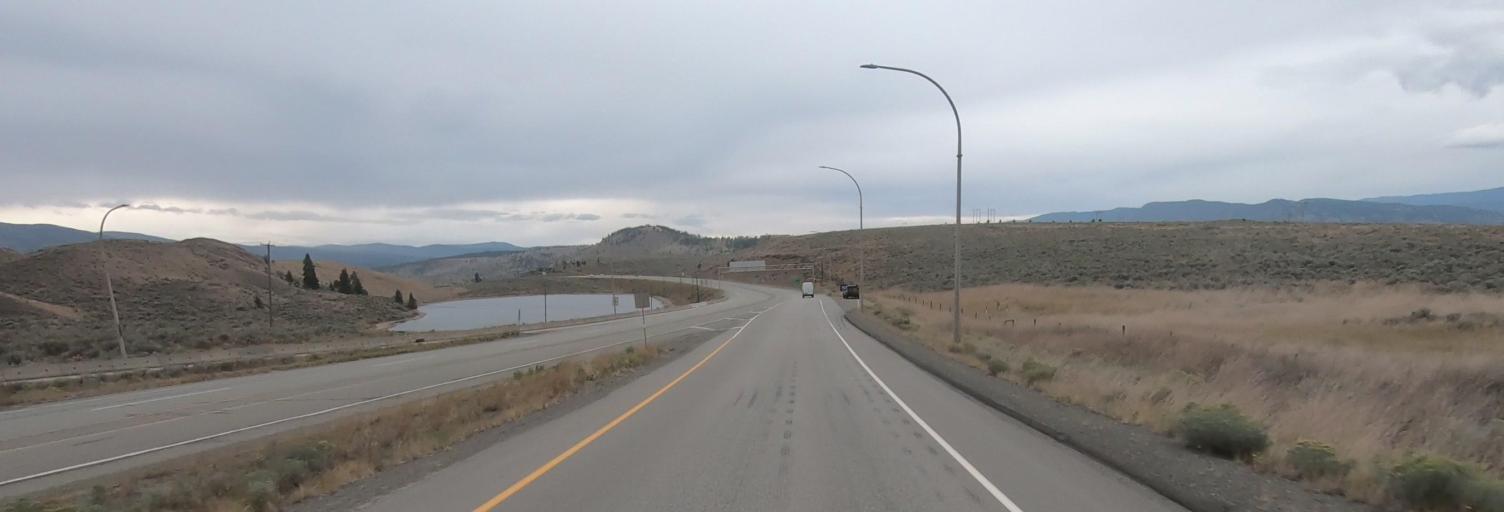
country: CA
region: British Columbia
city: Kamloops
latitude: 50.6673
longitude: -120.4602
